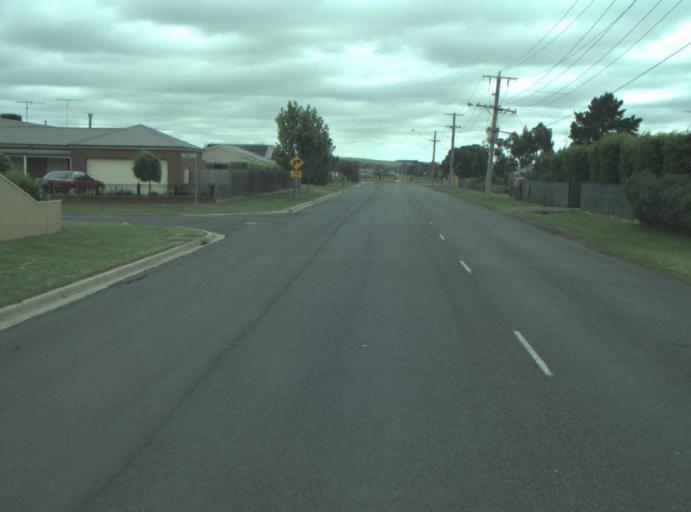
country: AU
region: Victoria
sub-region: Greater Geelong
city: Bell Post Hill
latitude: -38.0663
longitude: 144.3401
